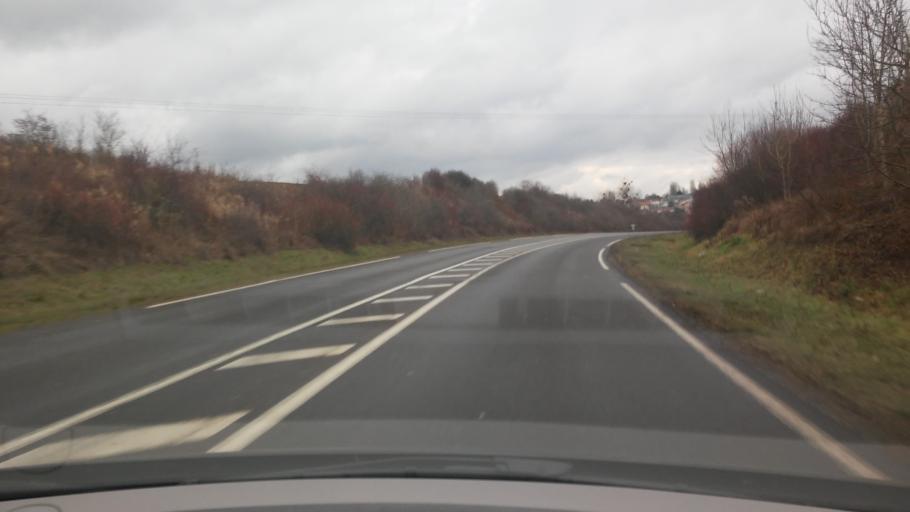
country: FR
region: Lorraine
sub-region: Departement de la Moselle
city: Peltre
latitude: 49.1189
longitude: 6.2540
